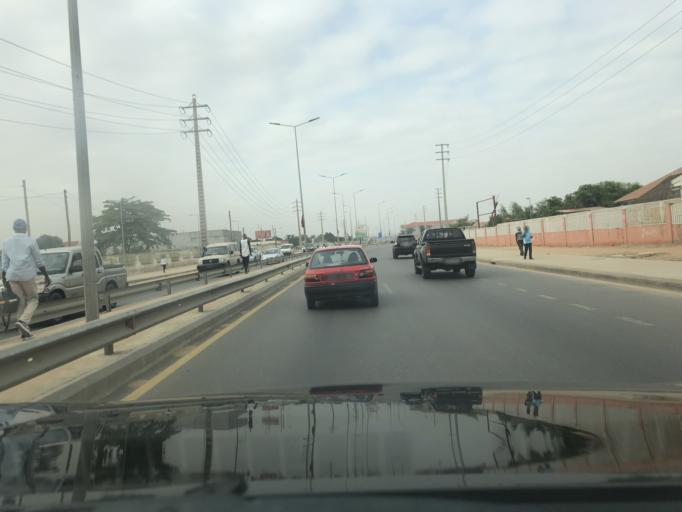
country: AO
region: Luanda
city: Luanda
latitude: -8.8919
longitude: 13.2594
